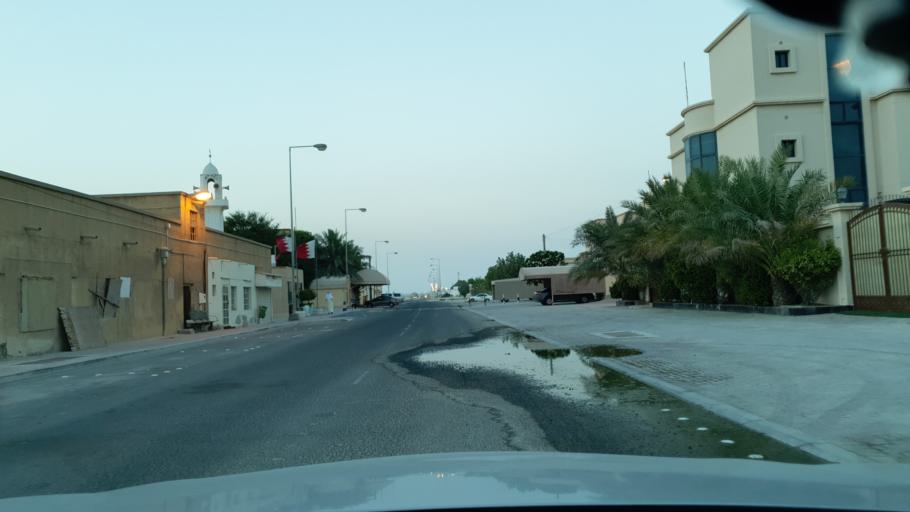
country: BH
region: Central Governorate
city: Dar Kulayb
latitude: 25.9787
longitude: 50.6152
